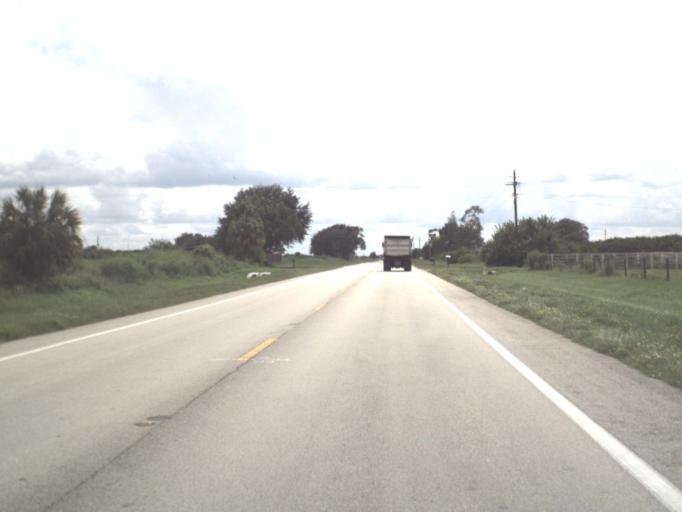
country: US
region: Florida
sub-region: DeSoto County
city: Southeast Arcadia
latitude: 27.1082
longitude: -81.7949
